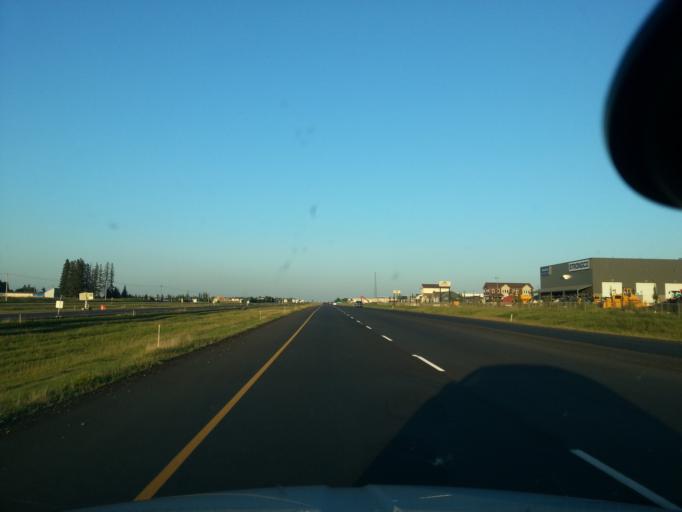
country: CA
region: Alberta
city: St. Albert
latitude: 53.5696
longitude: -113.7548
